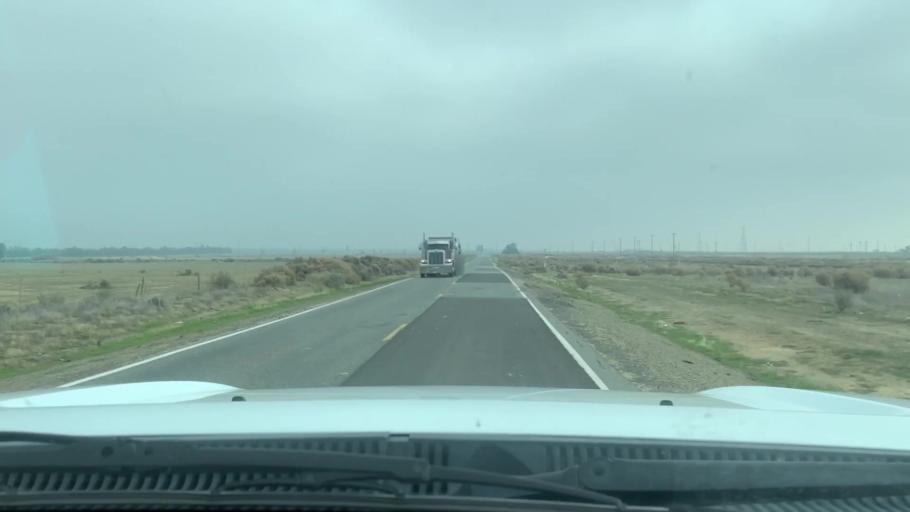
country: US
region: California
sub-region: Kern County
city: Lost Hills
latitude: 35.5481
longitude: -119.7855
